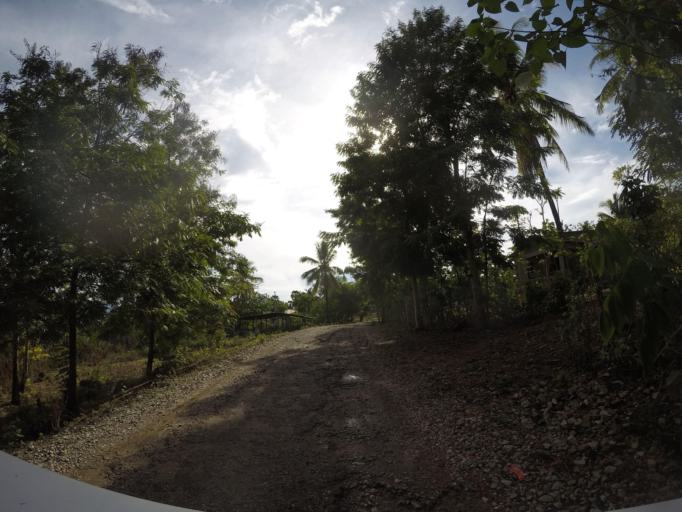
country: TL
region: Baucau
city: Baucau
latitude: -8.5004
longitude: 126.4598
